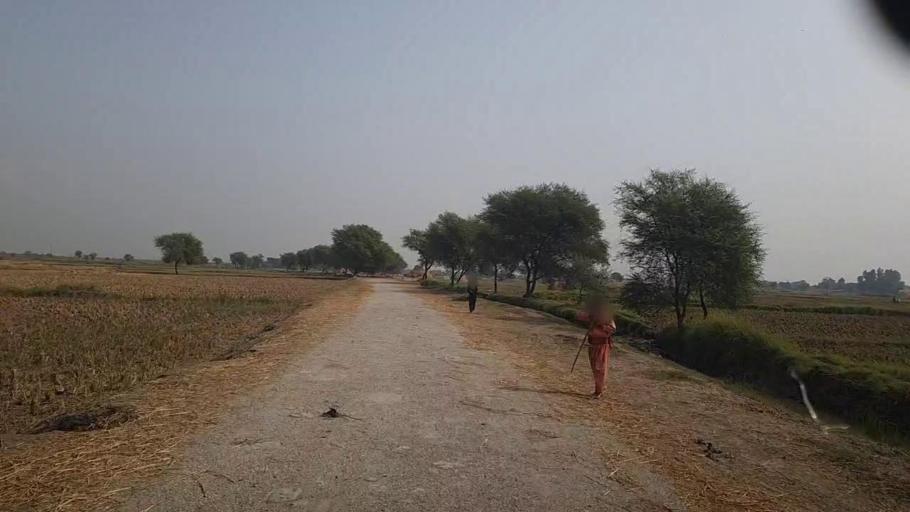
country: PK
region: Sindh
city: Kashmor
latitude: 28.3801
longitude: 69.4402
